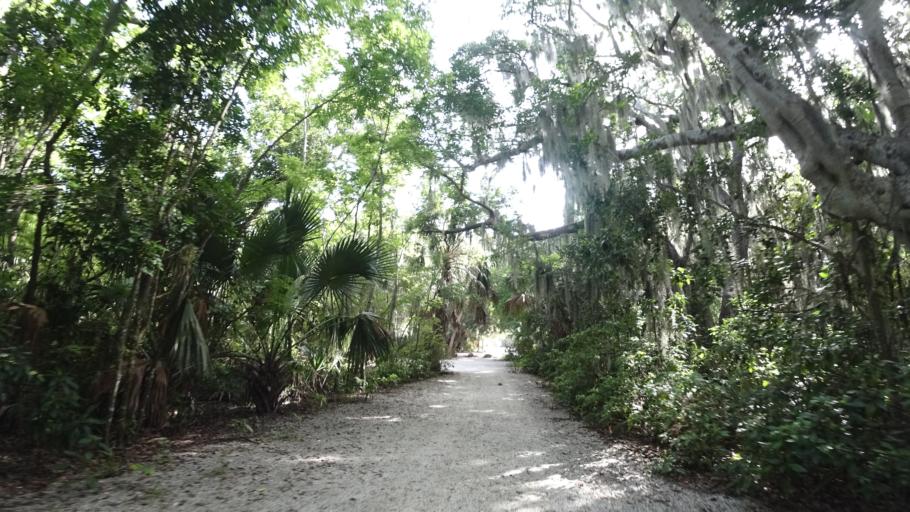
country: US
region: Florida
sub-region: Manatee County
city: West Bradenton
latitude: 27.5315
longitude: -82.6262
